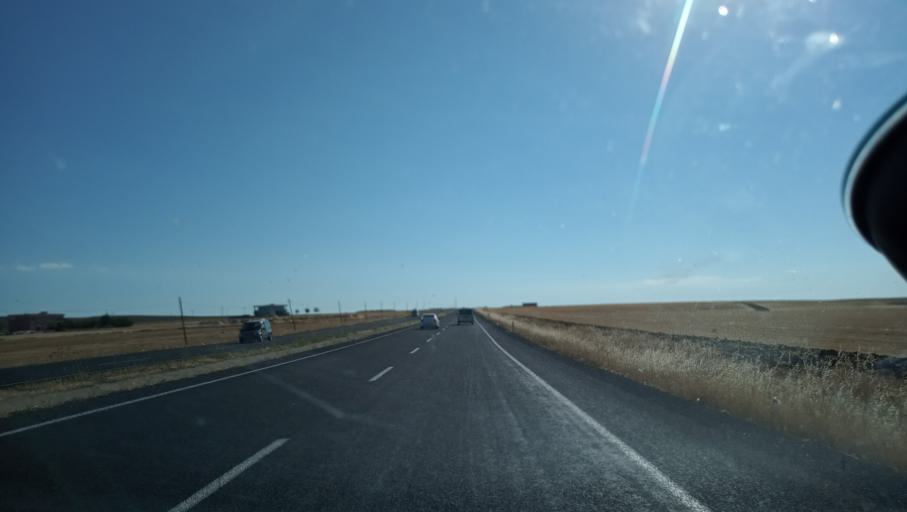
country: TR
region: Diyarbakir
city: Ambar
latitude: 38.0007
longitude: 40.4187
